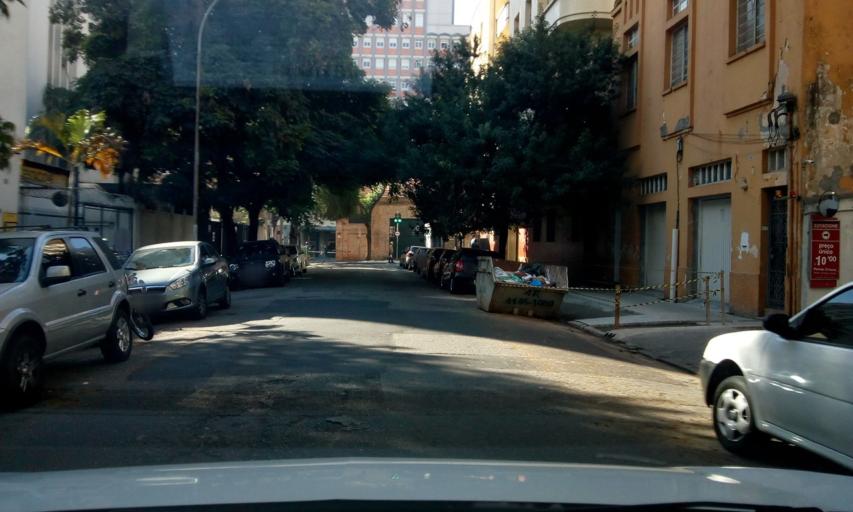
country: BR
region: Sao Paulo
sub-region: Sao Paulo
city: Sao Paulo
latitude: -23.5427
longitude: -46.6520
